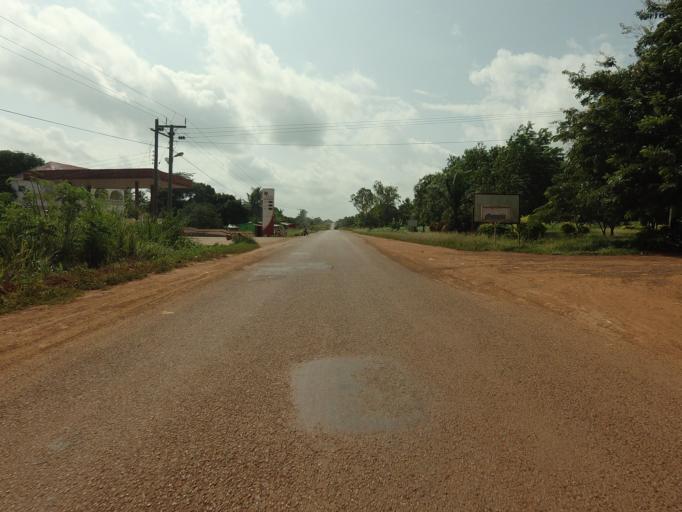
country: TG
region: Maritime
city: Tsevie
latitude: 6.3678
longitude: 0.8508
